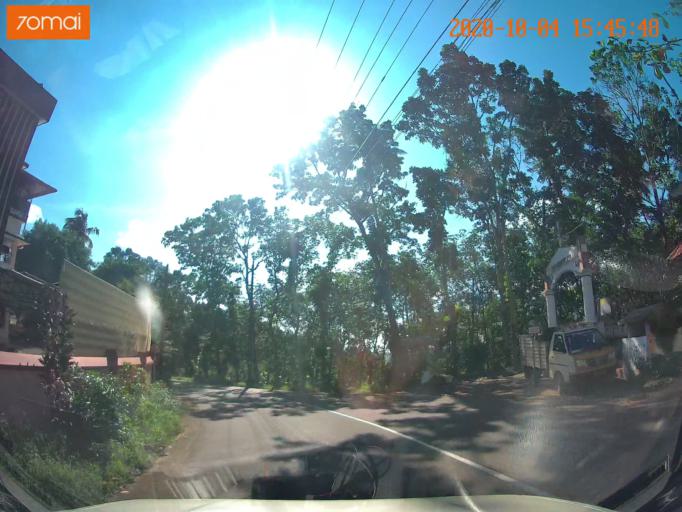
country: IN
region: Kerala
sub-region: Kottayam
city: Palackattumala
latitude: 9.7607
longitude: 76.5779
